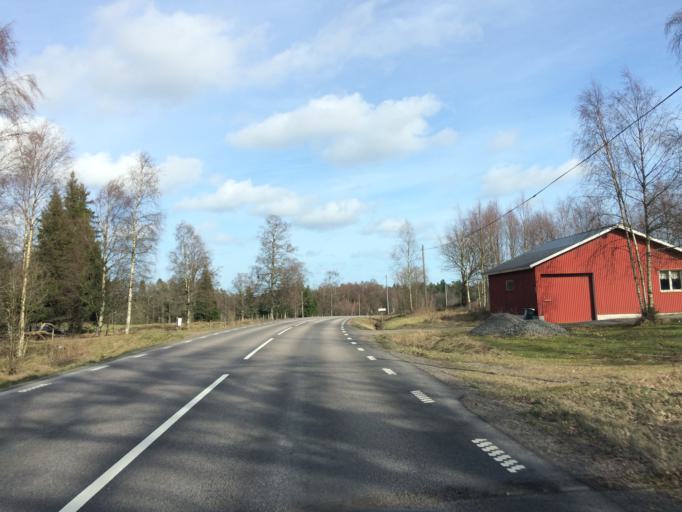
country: SE
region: Halland
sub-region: Hylte Kommun
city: Hyltebruk
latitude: 57.0254
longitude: 13.2197
